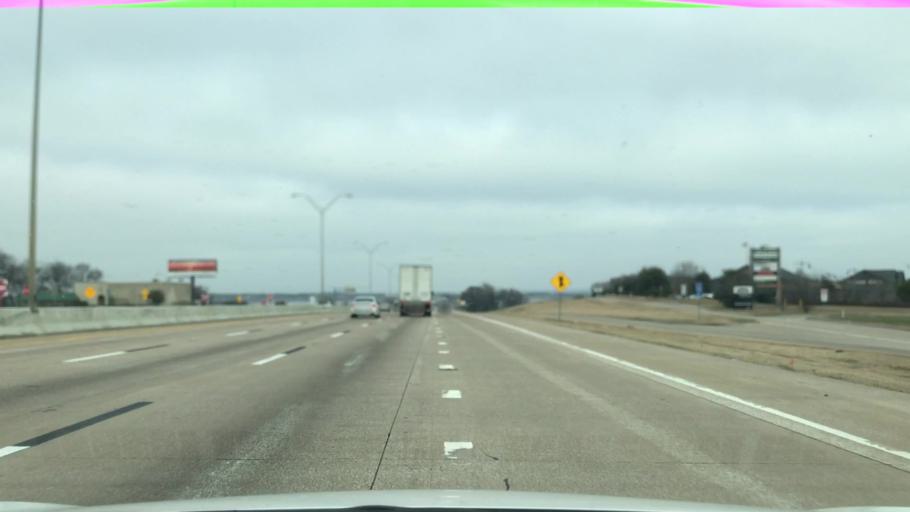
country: US
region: Texas
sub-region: Dallas County
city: Rowlett
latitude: 32.8653
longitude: -96.5426
